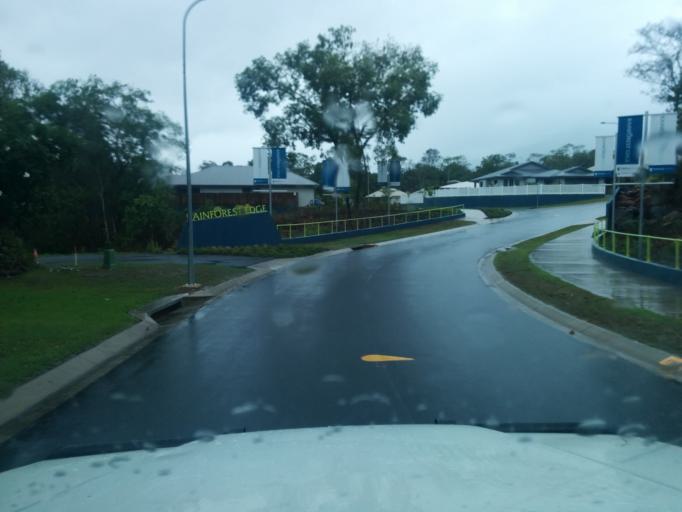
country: AU
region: Queensland
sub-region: Cairns
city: Woree
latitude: -16.9880
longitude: 145.7335
